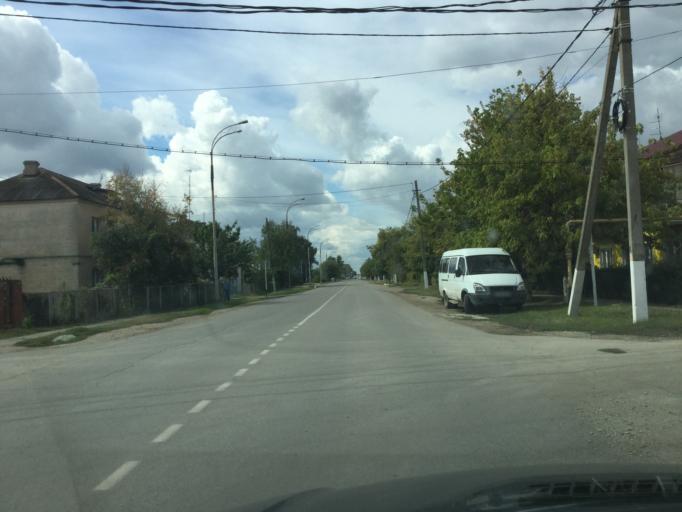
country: RU
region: Krasnodarskiy
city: Slavyansk-na-Kubani
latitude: 45.2536
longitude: 38.1112
